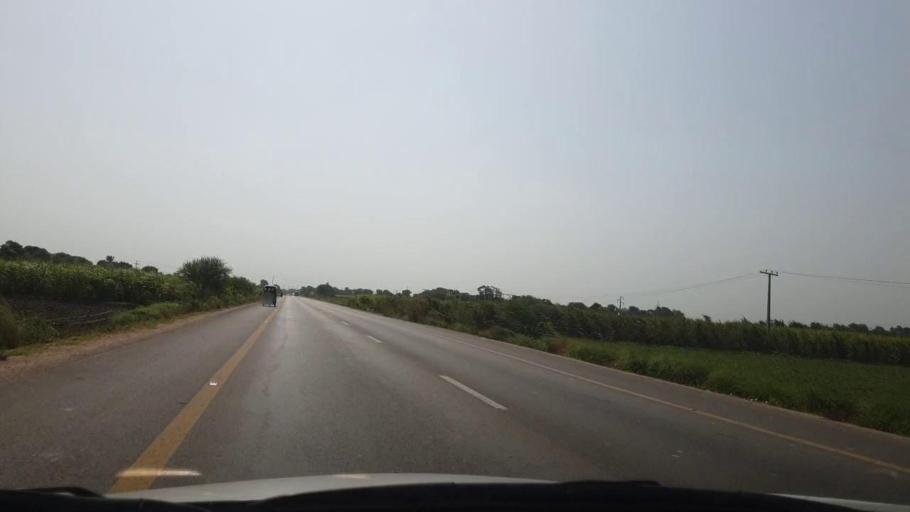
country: PK
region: Sindh
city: Matli
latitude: 25.0885
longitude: 68.6021
